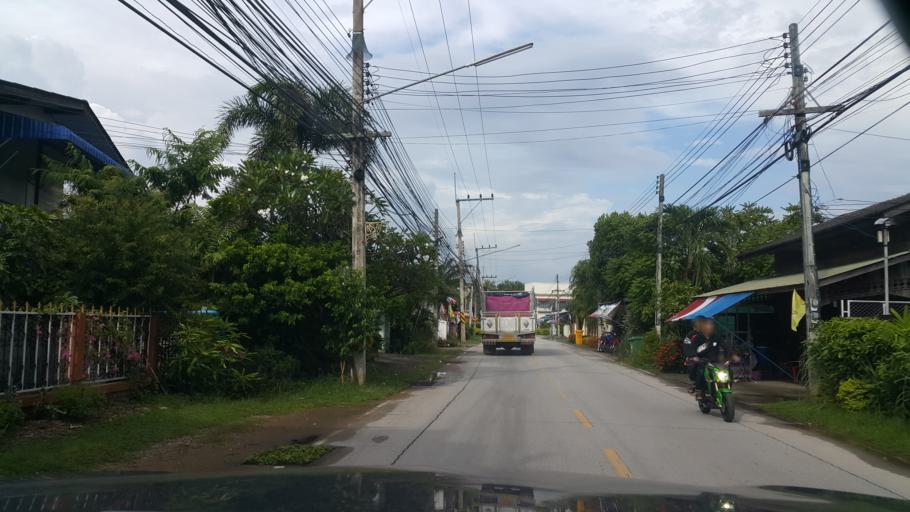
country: TH
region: Lampang
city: Thoen
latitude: 17.6117
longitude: 99.2170
